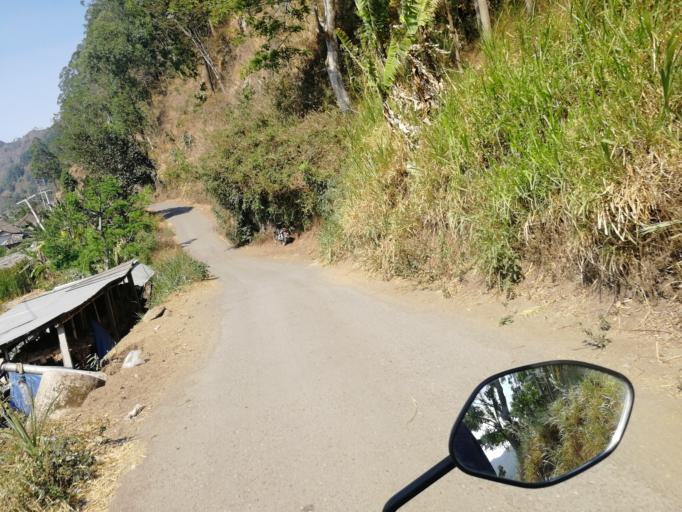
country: ID
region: Bali
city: Banjar Trunyan
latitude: -8.2698
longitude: 115.4180
